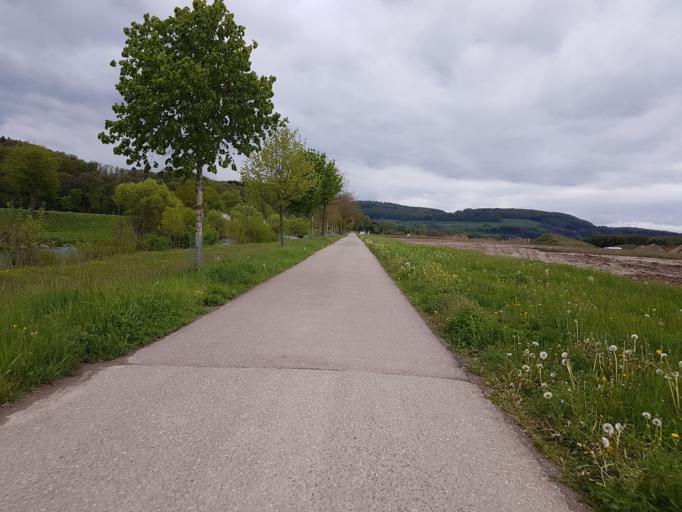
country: DE
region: Baden-Wuerttemberg
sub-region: Freiburg Region
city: Lauchringen
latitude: 47.6379
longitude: 8.3465
